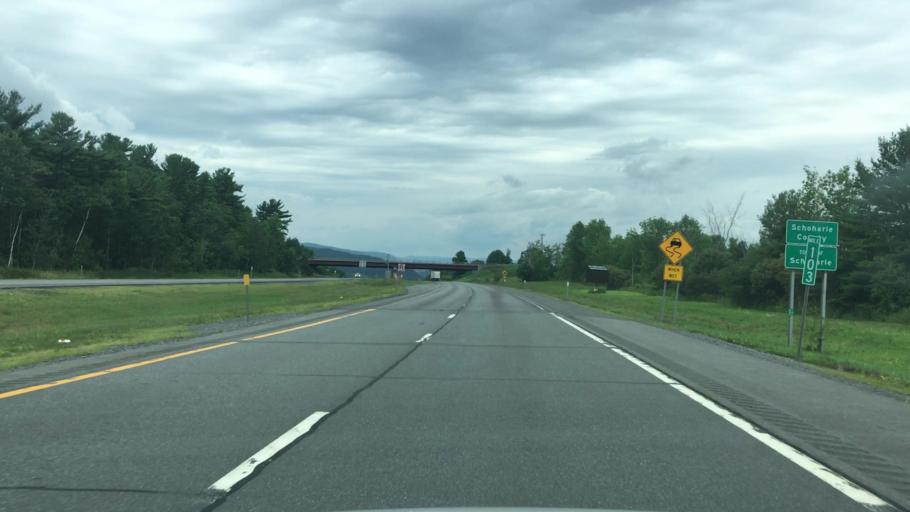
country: US
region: New York
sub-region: Schoharie County
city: Schoharie
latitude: 42.7149
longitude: -74.2718
